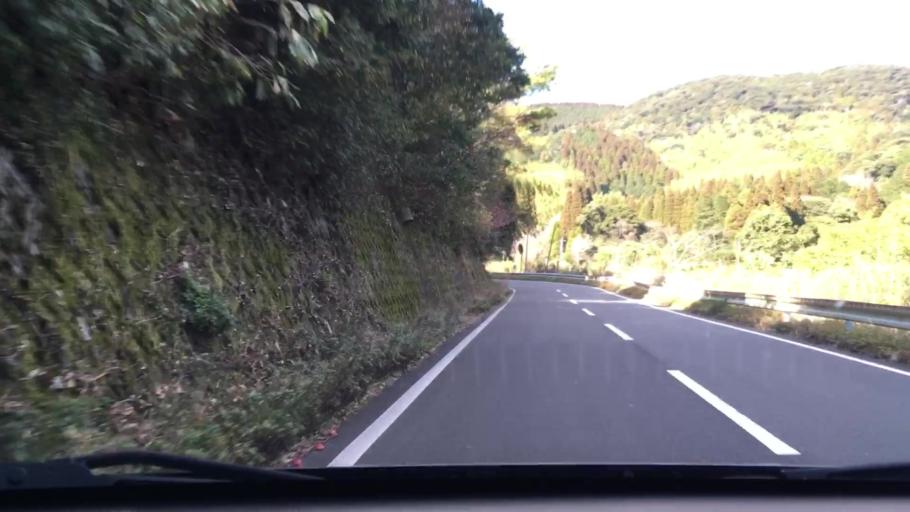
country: JP
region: Kagoshima
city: Ijuin
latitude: 31.7165
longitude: 130.4326
